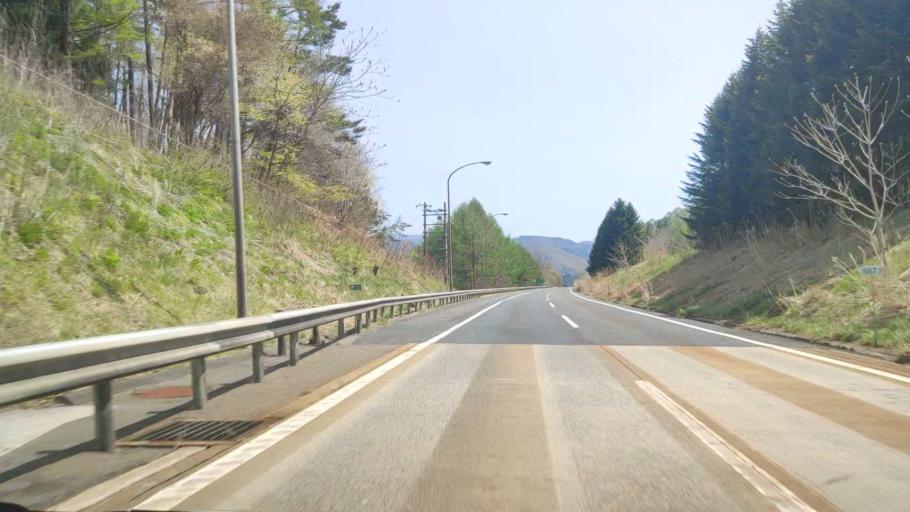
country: JP
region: Iwate
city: Ichinohe
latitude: 40.2264
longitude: 141.2687
